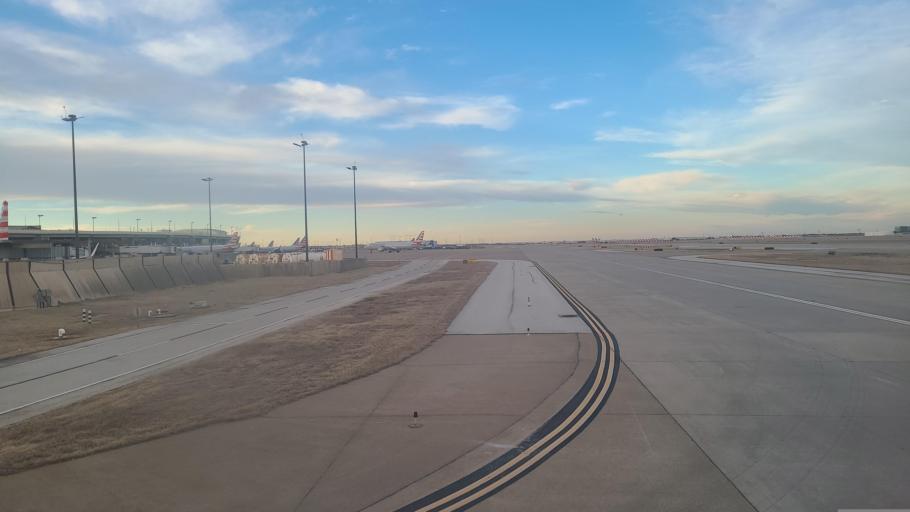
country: US
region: Texas
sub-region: Tarrant County
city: Grapevine
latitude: 32.9014
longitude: -97.0333
